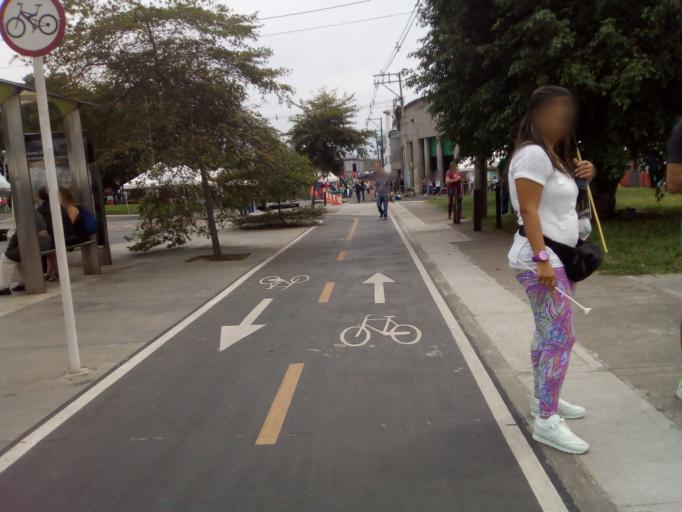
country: CO
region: Antioquia
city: Medellin
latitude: 6.2328
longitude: -75.5743
